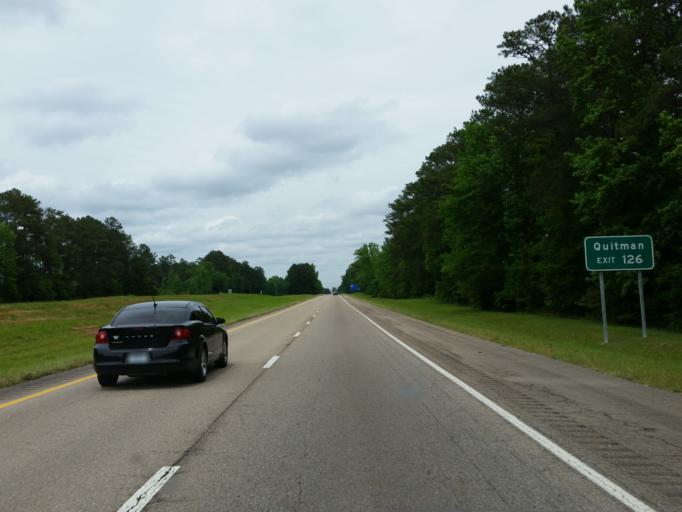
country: US
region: Mississippi
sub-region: Clarke County
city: Stonewall
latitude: 32.0496
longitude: -88.9155
